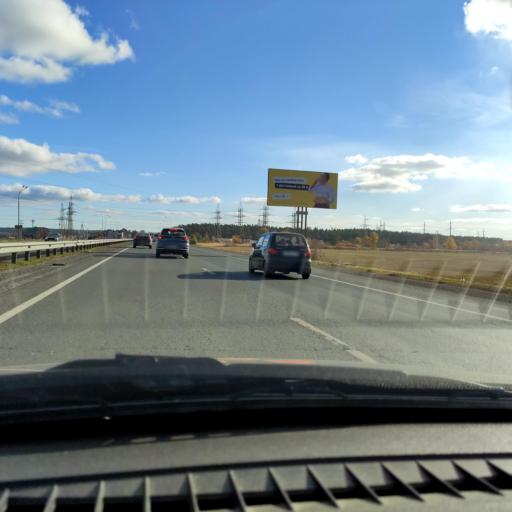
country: RU
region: Samara
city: Zhigulevsk
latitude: 53.5454
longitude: 49.5121
